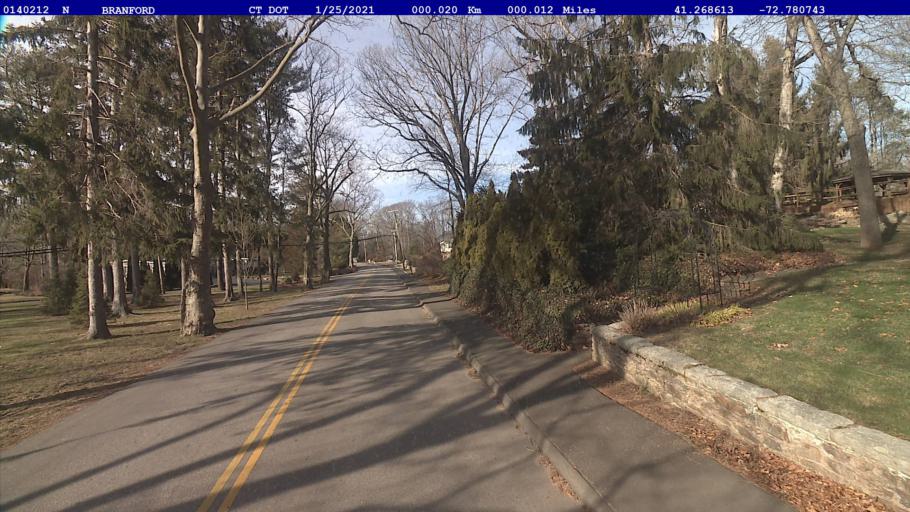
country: US
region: Connecticut
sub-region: New Haven County
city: Branford Center
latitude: 41.2686
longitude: -72.7807
